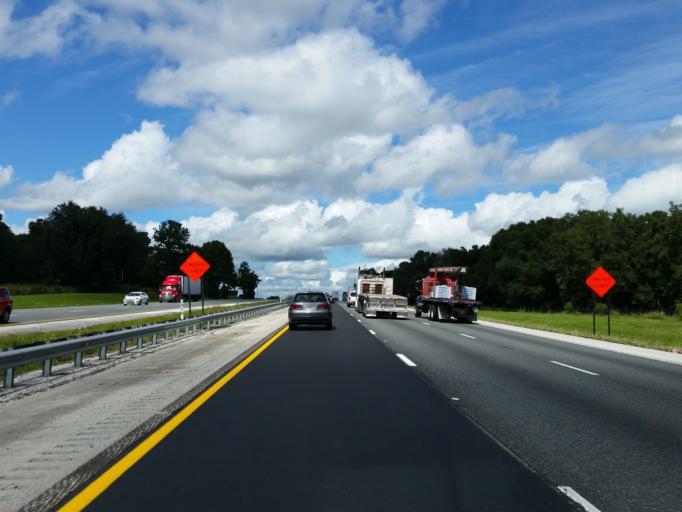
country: US
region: Florida
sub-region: Marion County
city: Ocala
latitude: 29.3072
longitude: -82.2075
